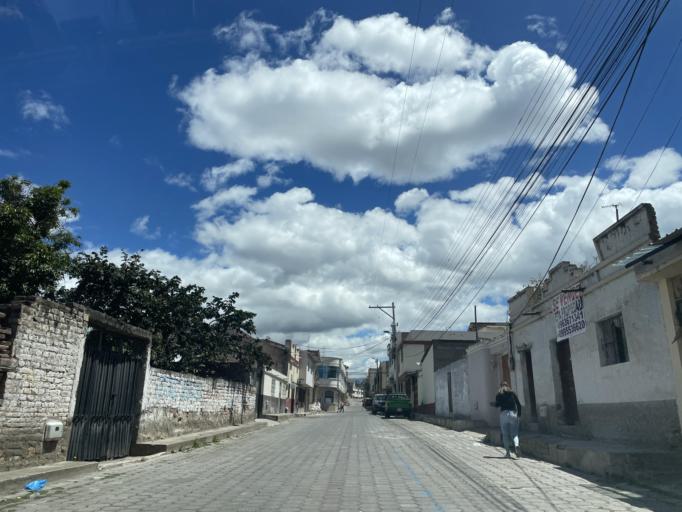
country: EC
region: Chimborazo
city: Guano
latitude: -1.6049
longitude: -78.6443
